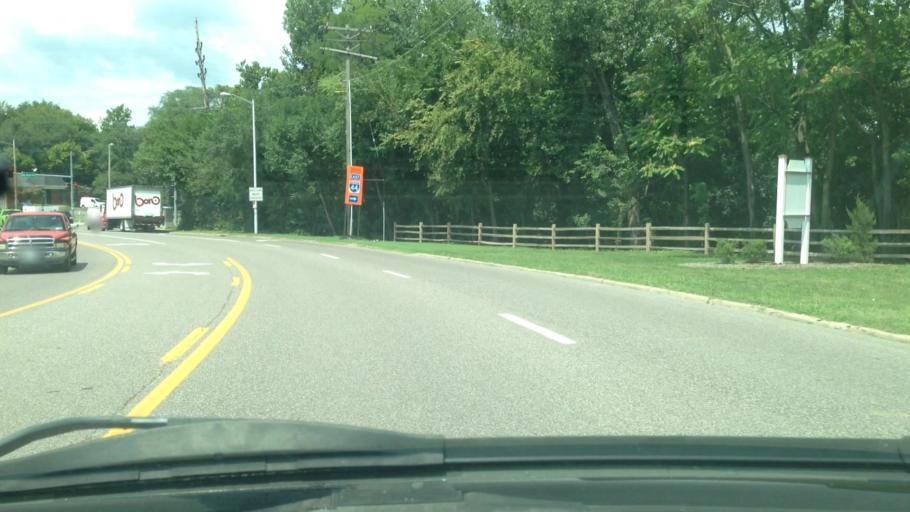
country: US
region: Missouri
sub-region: Saint Louis County
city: Maplewood
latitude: 38.6001
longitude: -90.3256
